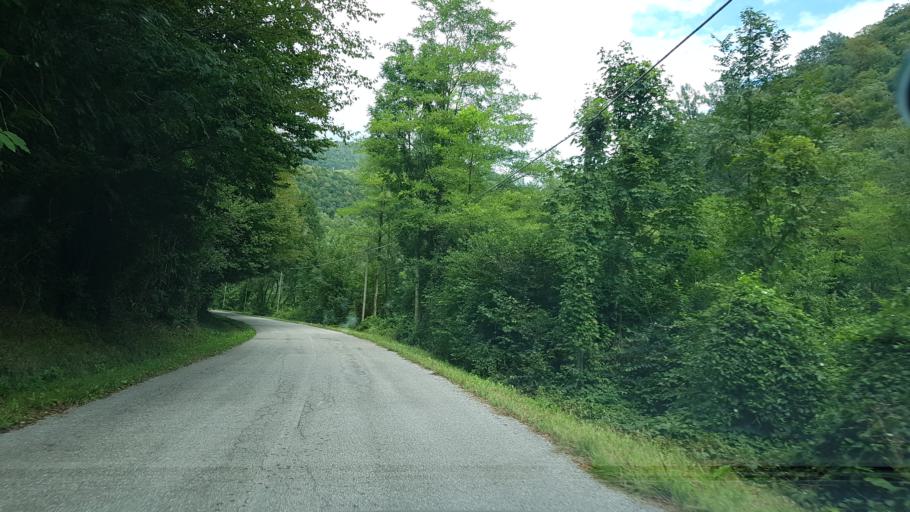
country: IT
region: Friuli Venezia Giulia
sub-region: Provincia di Udine
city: San Leonardo
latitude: 46.0786
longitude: 13.5427
